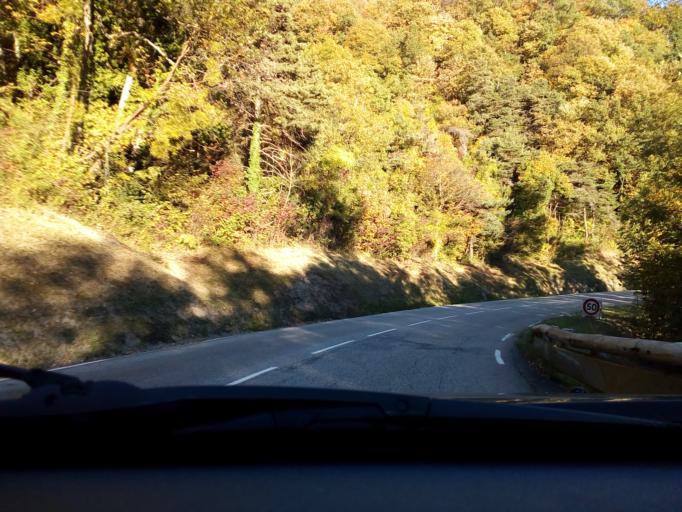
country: FR
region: Rhone-Alpes
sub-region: Departement de l'Isere
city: Corenc
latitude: 45.2304
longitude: 5.7538
